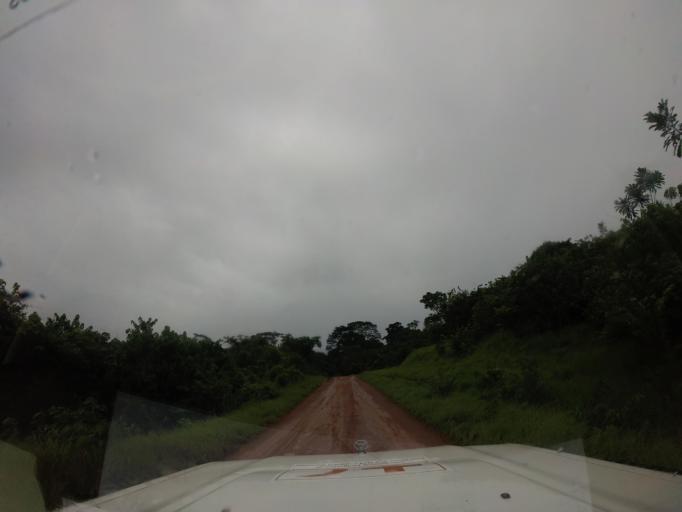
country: SL
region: Eastern Province
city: Kenema
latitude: 7.7193
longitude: -11.1895
